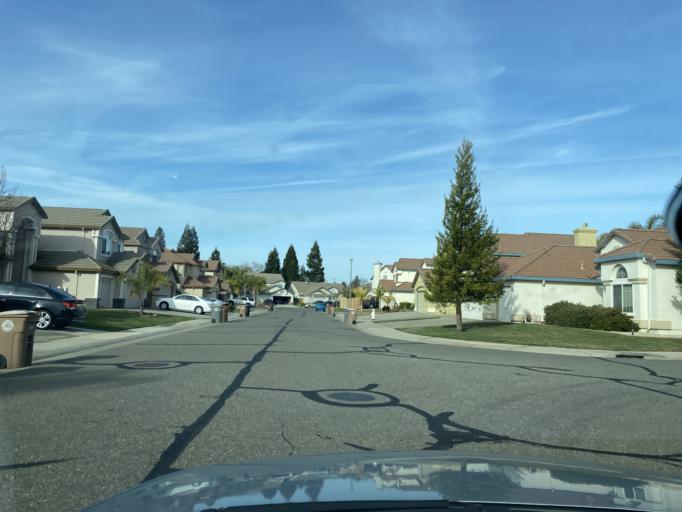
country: US
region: California
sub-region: Sacramento County
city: Elk Grove
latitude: 38.4398
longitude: -121.3777
